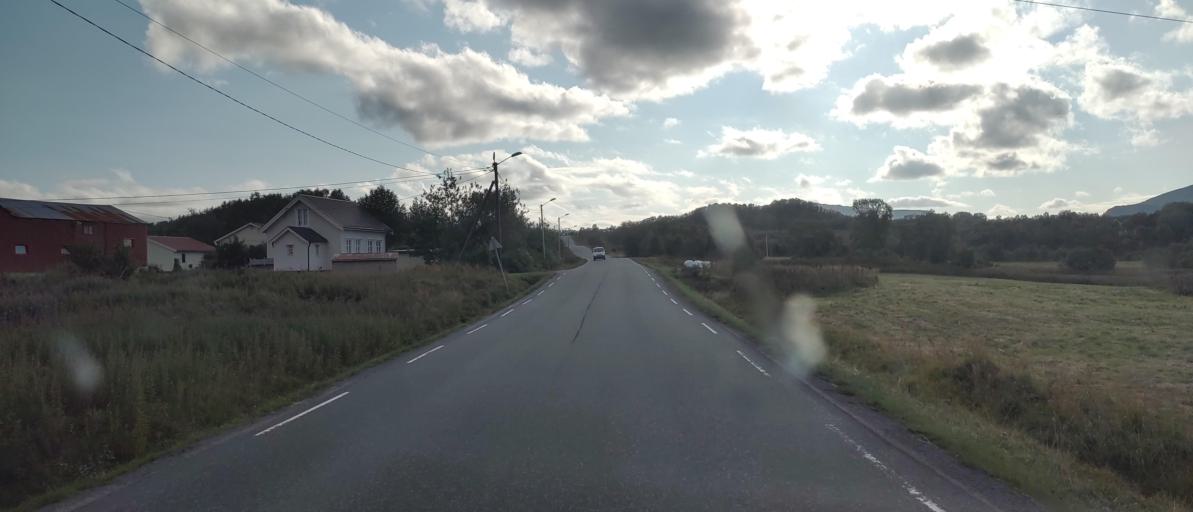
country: NO
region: Nordland
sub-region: Sortland
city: Sortland
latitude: 68.7244
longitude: 15.4737
